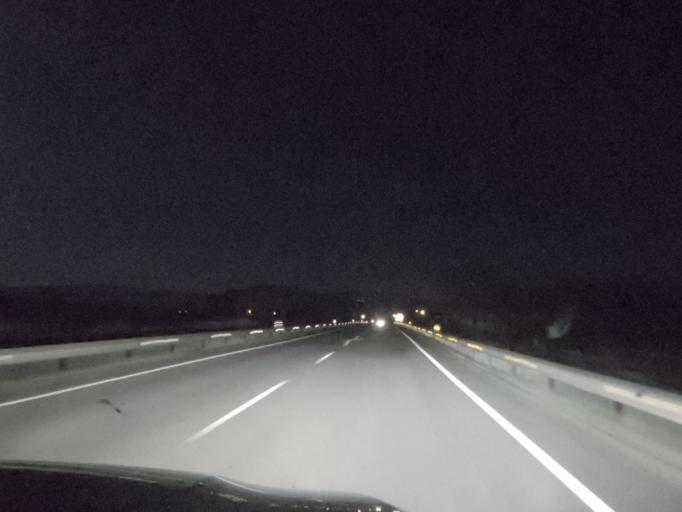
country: ES
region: Galicia
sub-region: Provincia de Ourense
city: Verin
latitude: 41.9502
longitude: -7.4931
